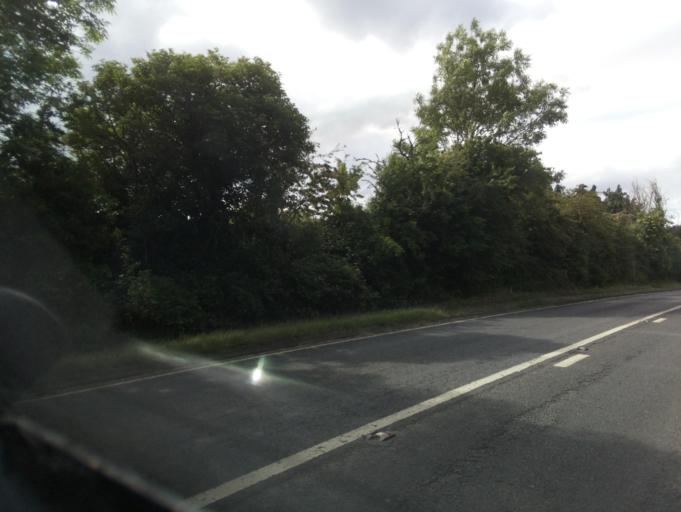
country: GB
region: England
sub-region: Worcestershire
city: Pershore
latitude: 52.1454
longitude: -2.1400
